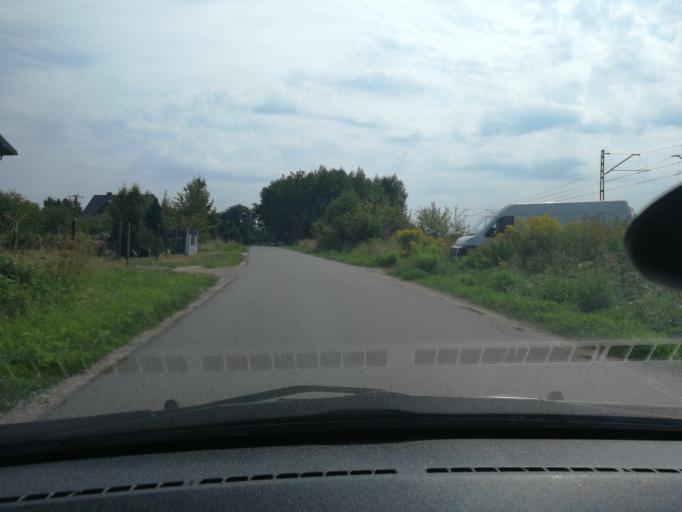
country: PL
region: Lodz Voivodeship
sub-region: Skierniewice
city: Skierniewice
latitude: 51.9751
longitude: 20.1070
